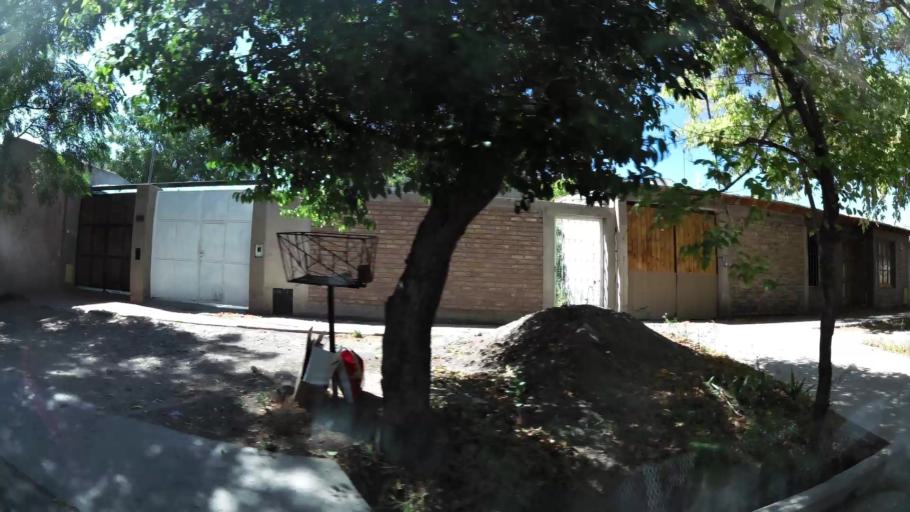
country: AR
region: Mendoza
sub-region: Departamento de Godoy Cruz
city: Godoy Cruz
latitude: -32.9509
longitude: -68.8412
